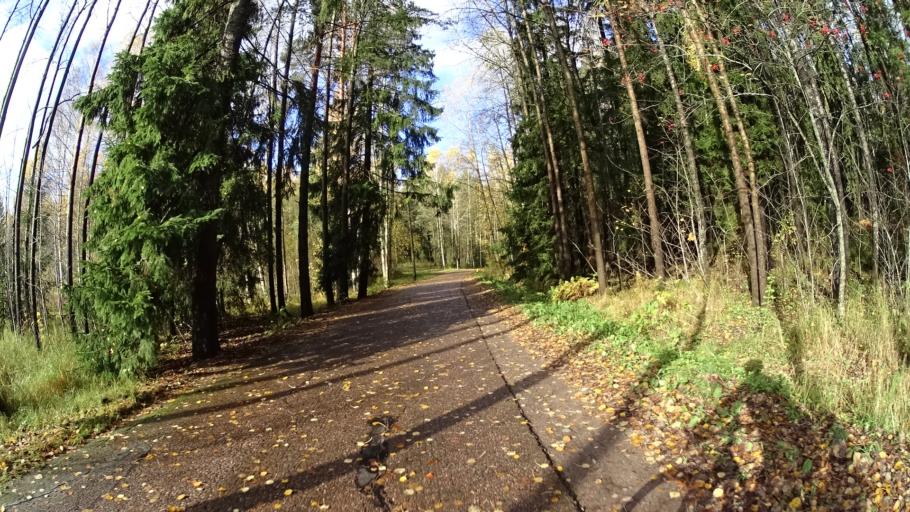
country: FI
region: Uusimaa
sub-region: Helsinki
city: Kilo
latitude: 60.2733
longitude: 24.8295
